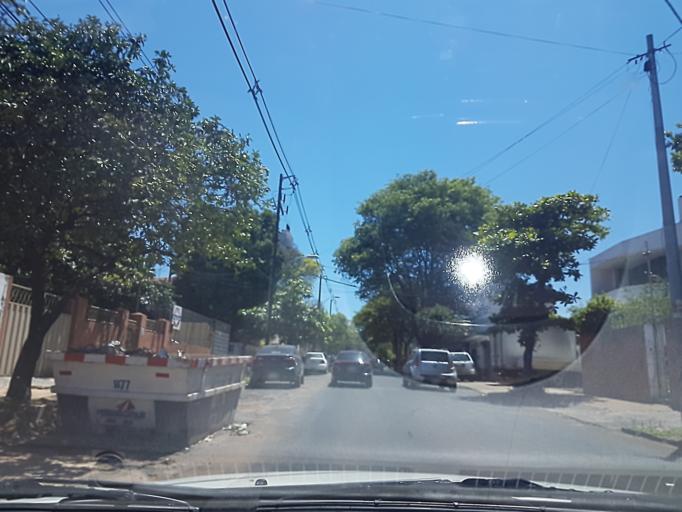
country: PY
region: Asuncion
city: Asuncion
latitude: -25.3053
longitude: -57.5996
